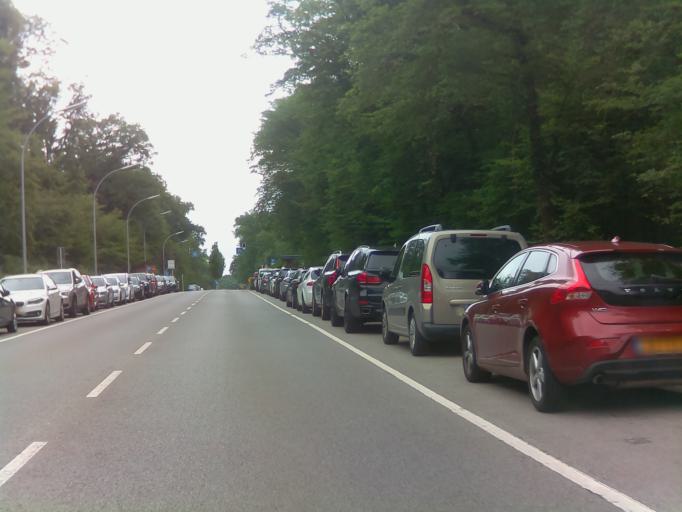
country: LU
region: Luxembourg
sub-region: Canton d'Esch-sur-Alzette
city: Bettembourg
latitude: 49.5103
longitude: 6.1166
